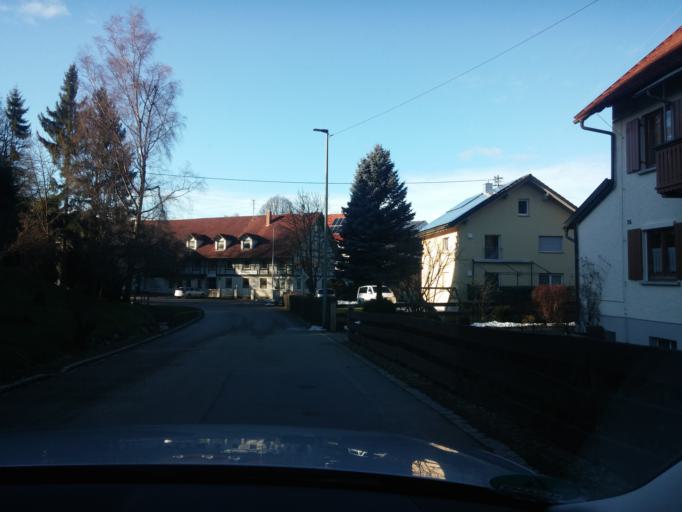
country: DE
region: Bavaria
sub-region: Swabia
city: Lautrach
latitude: 47.8899
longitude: 10.1375
